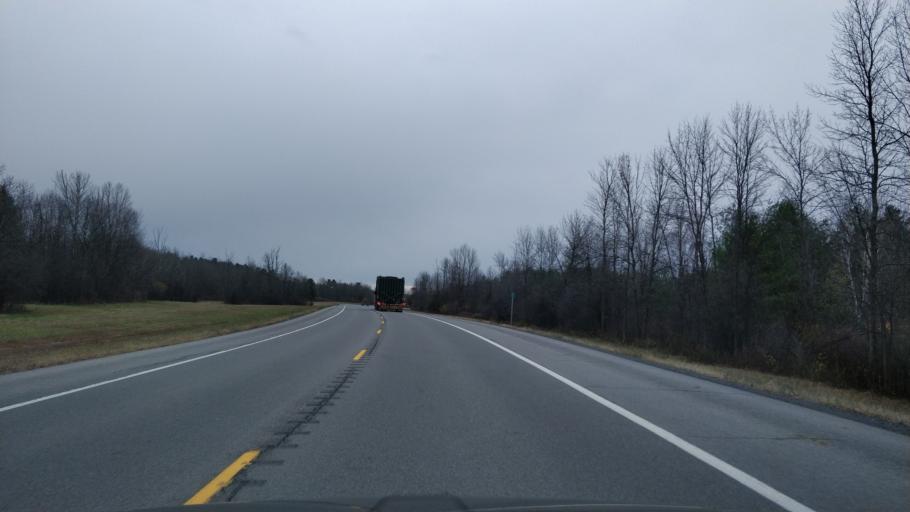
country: CA
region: Ontario
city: Brockville
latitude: 44.5879
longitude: -75.6404
